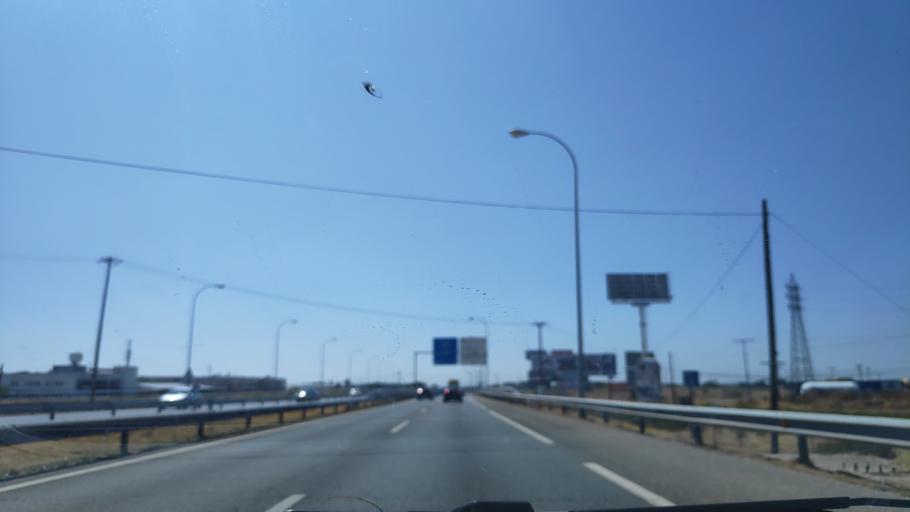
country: ES
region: Madrid
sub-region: Provincia de Madrid
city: Parla
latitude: 40.2299
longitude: -3.7833
